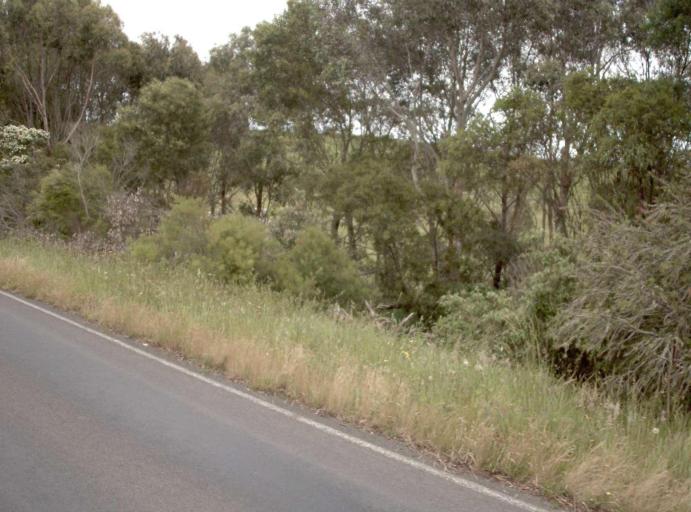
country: AU
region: Victoria
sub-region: Bass Coast
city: North Wonthaggi
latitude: -38.4514
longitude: 145.7984
